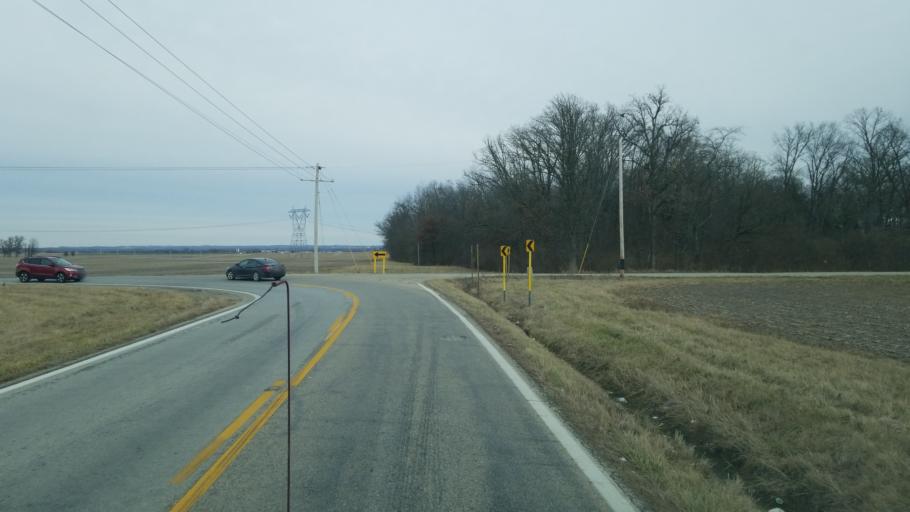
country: US
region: Ohio
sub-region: Pickaway County
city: Logan Elm Village
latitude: 39.5836
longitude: -83.0296
